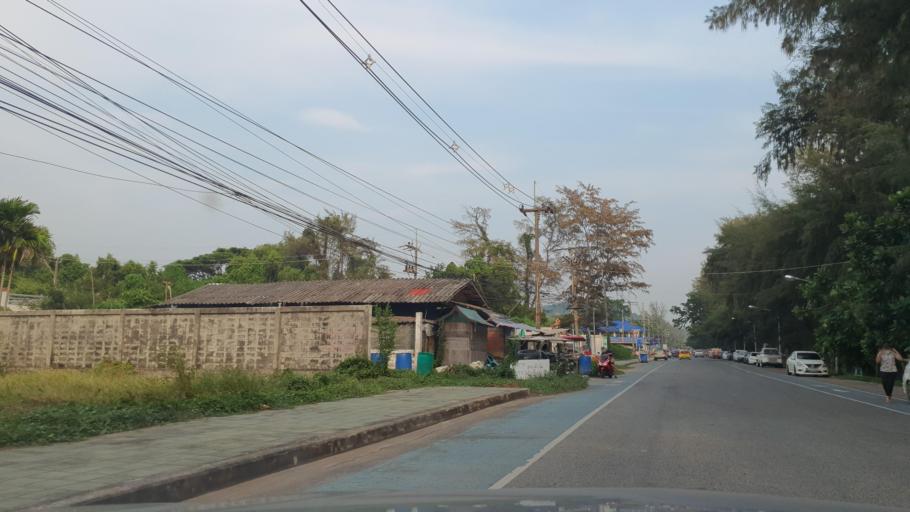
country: TH
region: Rayong
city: Rayong
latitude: 12.5996
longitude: 101.4054
